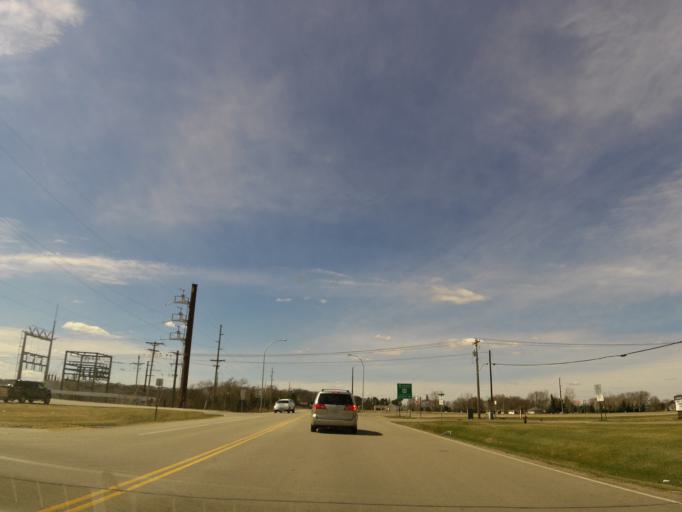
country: US
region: Minnesota
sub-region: Goodhue County
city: Cannon Falls
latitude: 44.5070
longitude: -92.9164
